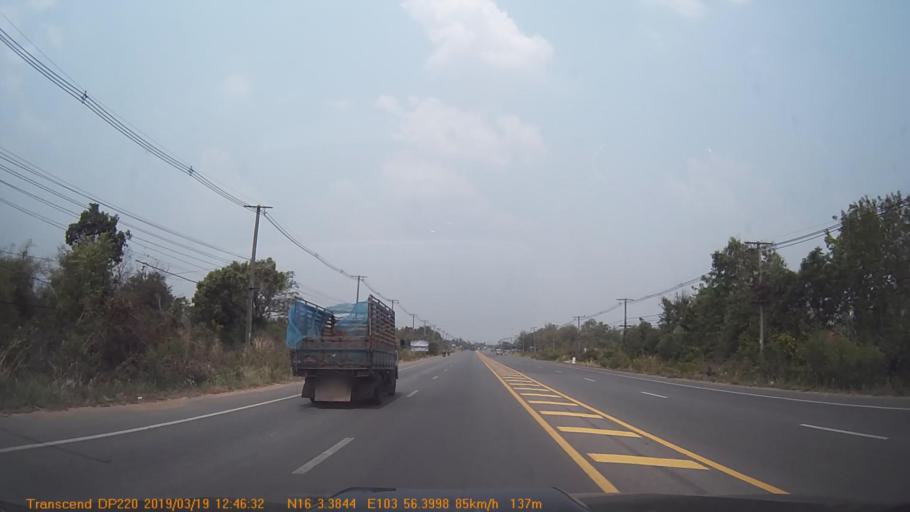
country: TH
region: Roi Et
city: Selaphum
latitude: 16.0568
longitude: 103.9401
